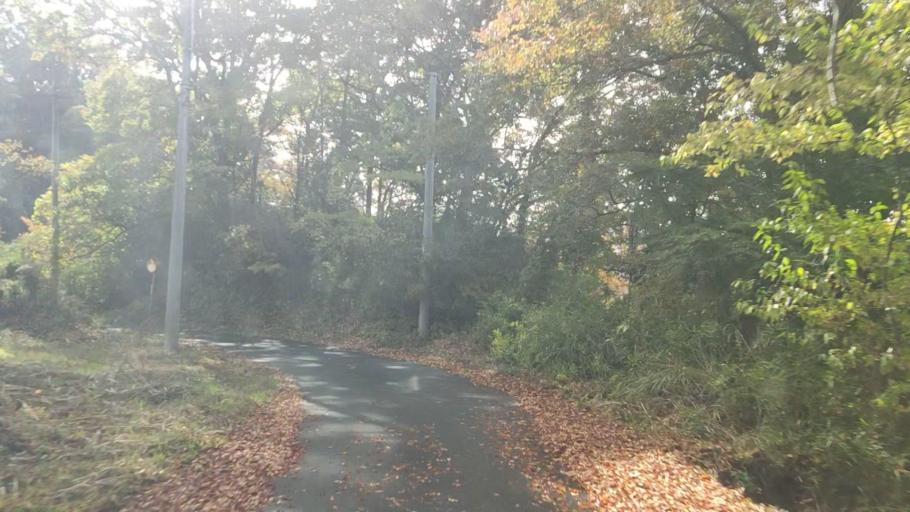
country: JP
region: Yamanashi
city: Ryuo
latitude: 35.4719
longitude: 138.4473
